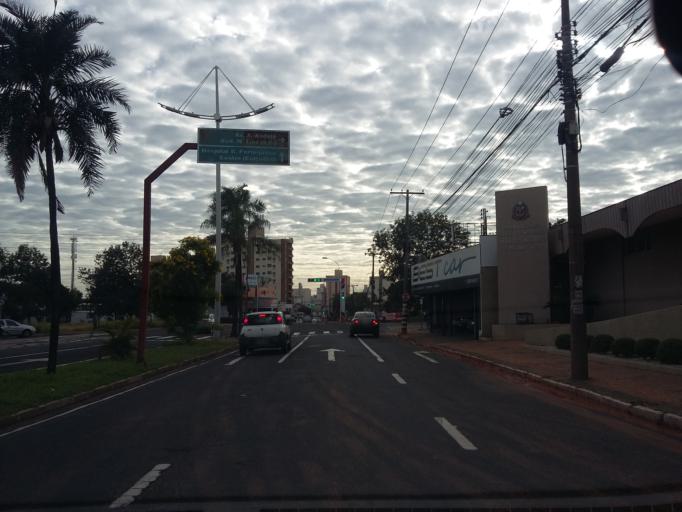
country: BR
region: Sao Paulo
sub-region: Sao Jose Do Rio Preto
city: Sao Jose do Rio Preto
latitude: -20.8242
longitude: -49.3935
